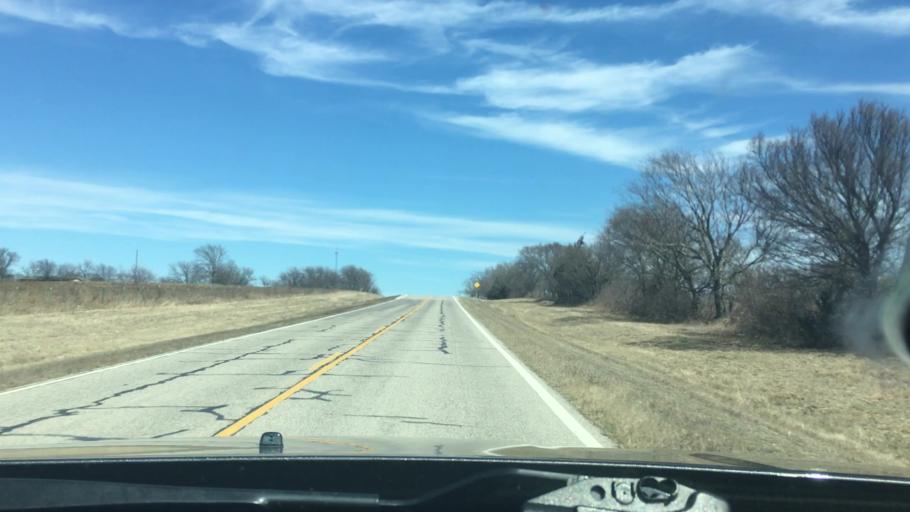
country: US
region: Oklahoma
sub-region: Carter County
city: Dickson
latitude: 34.3302
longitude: -96.9537
